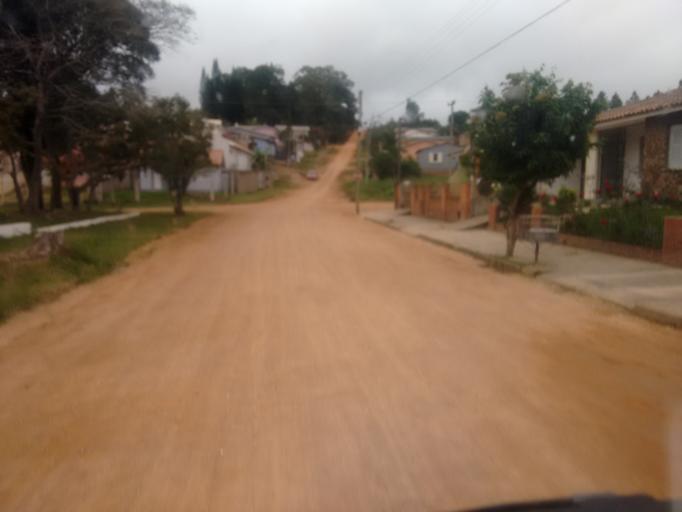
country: BR
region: Rio Grande do Sul
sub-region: Camaqua
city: Camaqua
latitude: -30.8348
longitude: -51.8160
